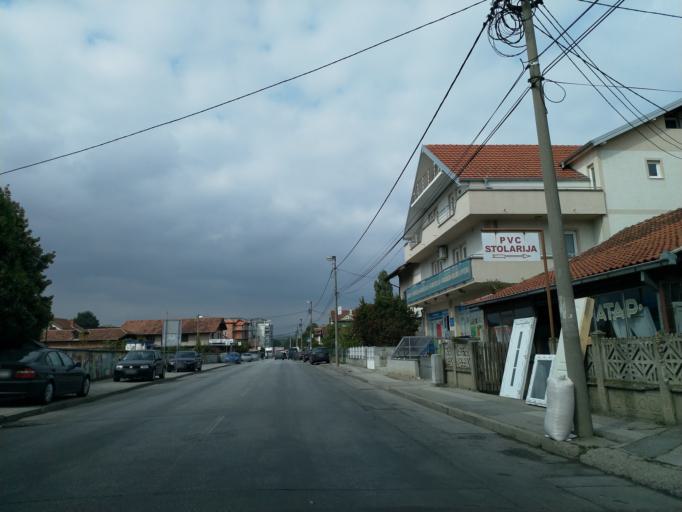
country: RS
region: Central Serbia
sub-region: Pomoravski Okrug
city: Jagodina
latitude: 43.9848
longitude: 21.2540
